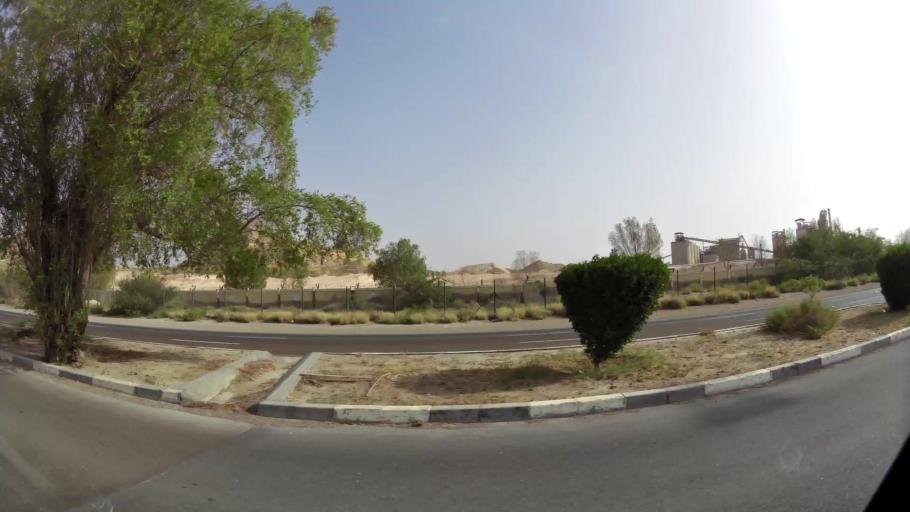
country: AE
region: Abu Dhabi
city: Al Ain
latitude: 24.1325
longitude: 55.7312
